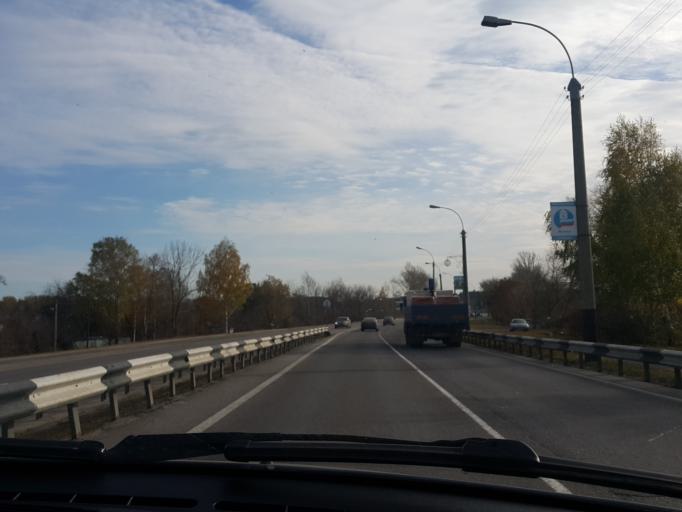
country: RU
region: Tambov
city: Tambov
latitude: 52.7189
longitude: 41.5006
